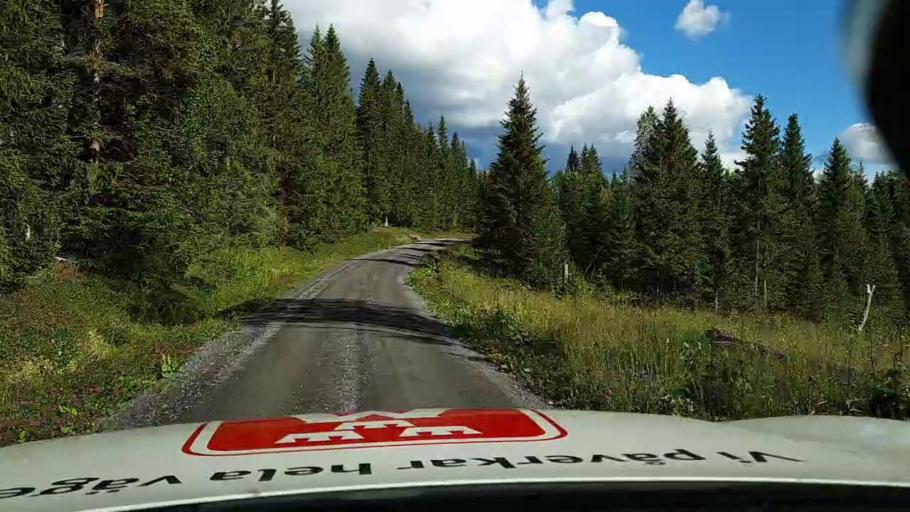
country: SE
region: Jaemtland
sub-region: Krokoms Kommun
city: Valla
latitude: 63.3178
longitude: 13.7693
